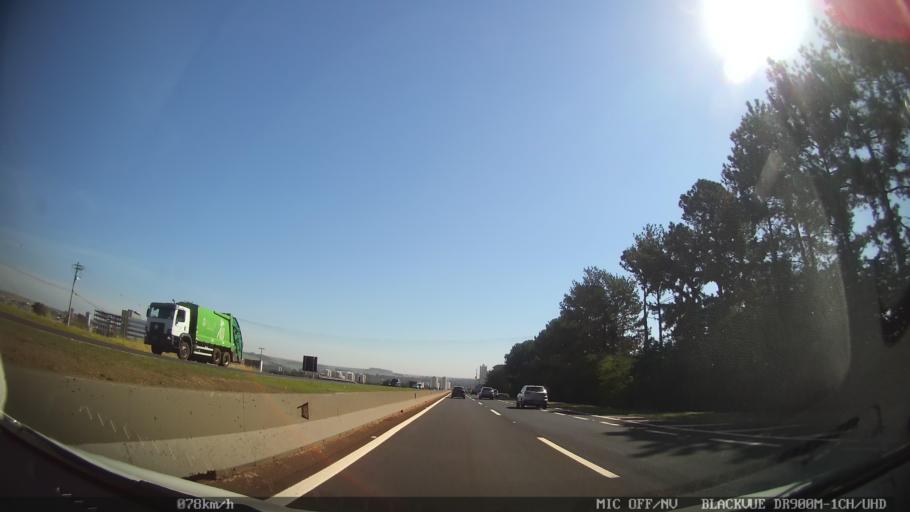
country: BR
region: Sao Paulo
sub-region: Ribeirao Preto
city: Ribeirao Preto
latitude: -21.2241
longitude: -47.8129
